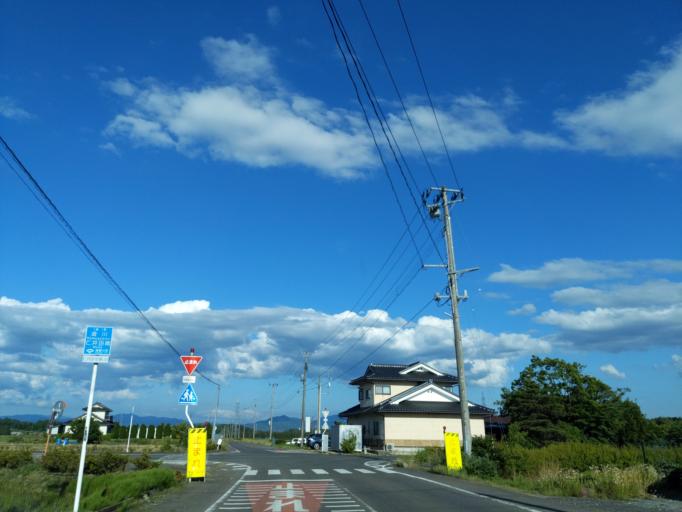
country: JP
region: Fukushima
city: Sukagawa
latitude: 37.3280
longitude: 140.3288
